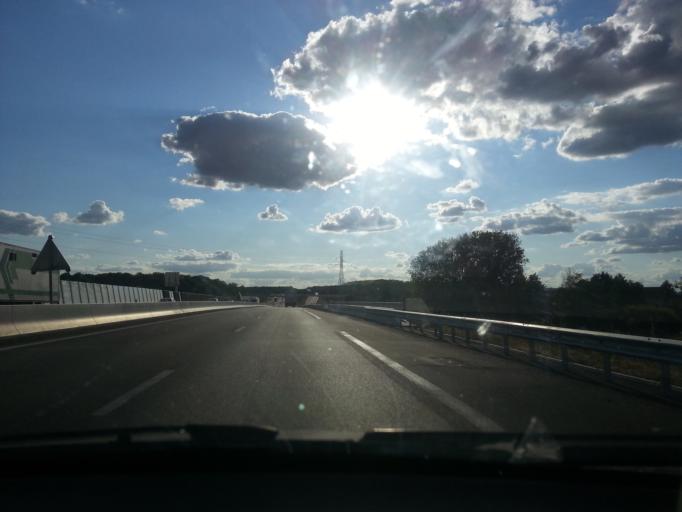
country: FR
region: Bourgogne
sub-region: Departement de Saone-et-Loire
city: Saint-Remy
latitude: 46.7555
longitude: 4.8231
